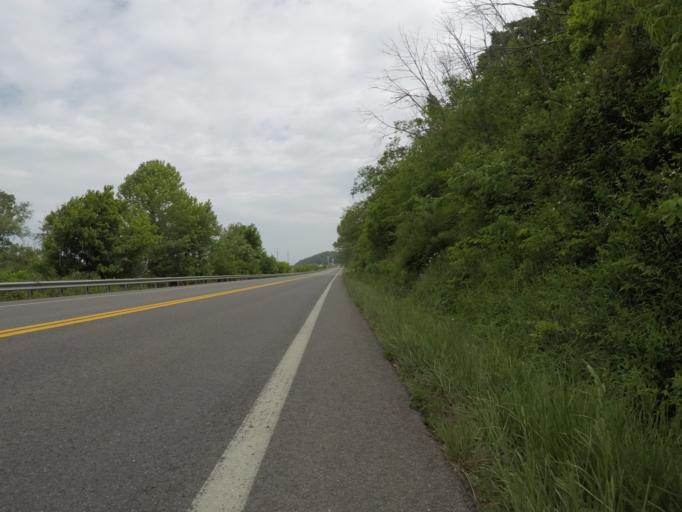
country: US
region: West Virginia
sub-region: Wayne County
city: Kenova
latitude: 38.3645
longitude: -82.5927
